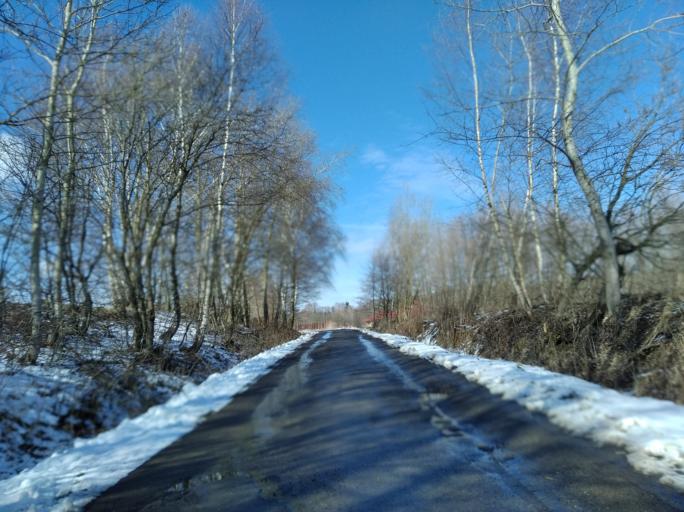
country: PL
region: Subcarpathian Voivodeship
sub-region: Powiat brzozowski
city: Jablonica Polska
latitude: 49.7275
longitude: 21.8738
